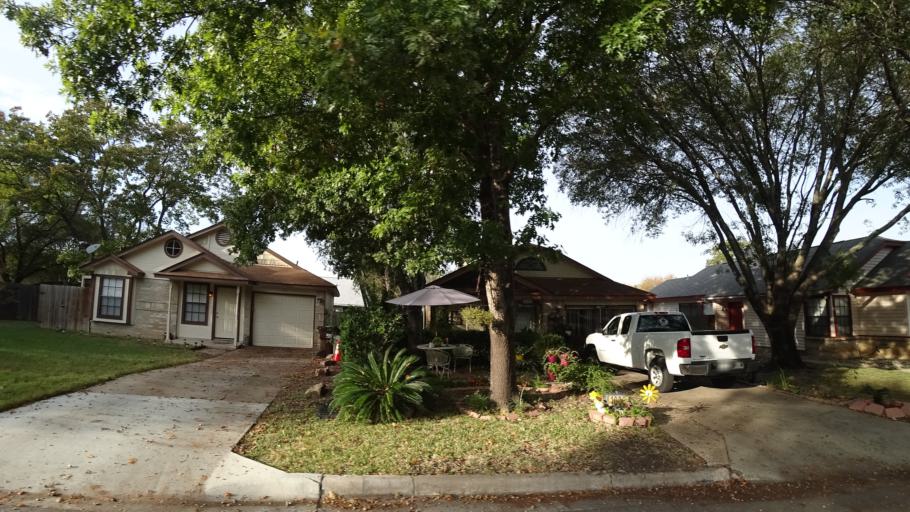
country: US
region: Texas
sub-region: Williamson County
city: Round Rock
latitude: 30.5002
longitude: -97.6663
